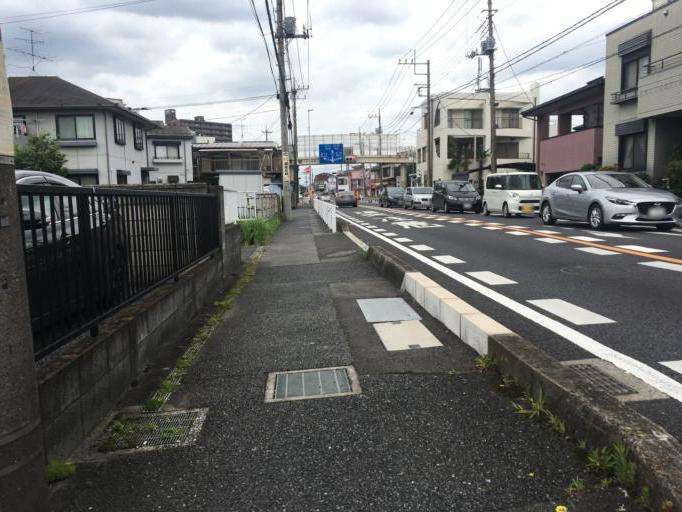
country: JP
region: Saitama
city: Kasukabe
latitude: 35.9790
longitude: 139.7630
